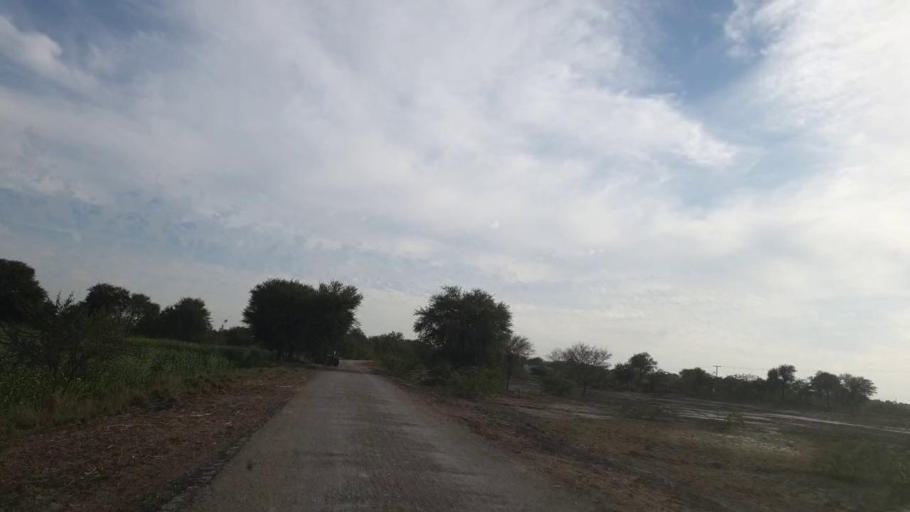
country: PK
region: Sindh
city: Pithoro
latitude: 25.6417
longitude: 69.3614
